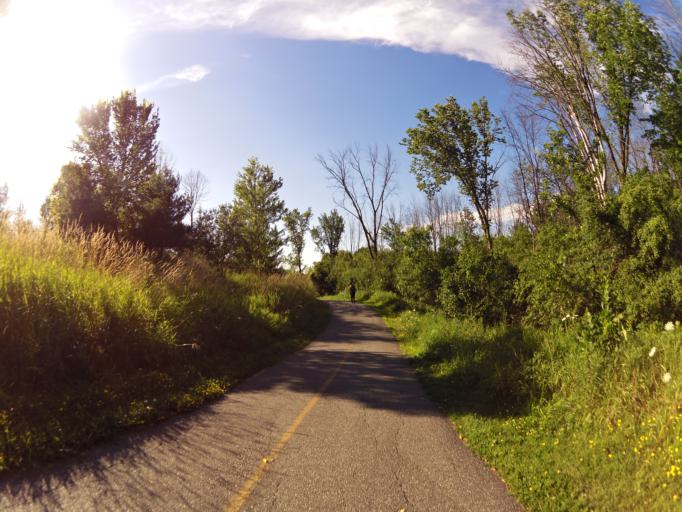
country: CA
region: Quebec
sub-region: Outaouais
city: Gatineau
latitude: 45.4672
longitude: -75.7320
